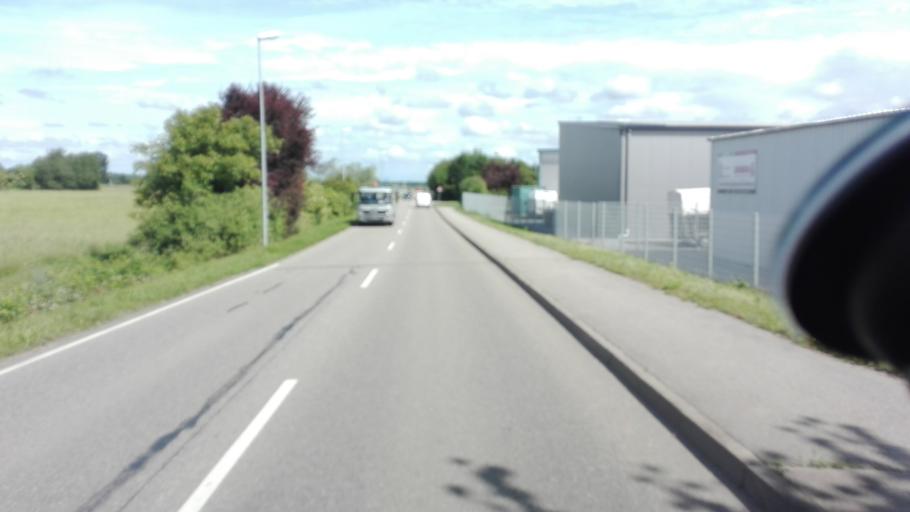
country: DE
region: Baden-Wuerttemberg
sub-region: Karlsruhe Region
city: Karlsdorf-Neuthard
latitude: 49.1465
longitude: 8.5467
